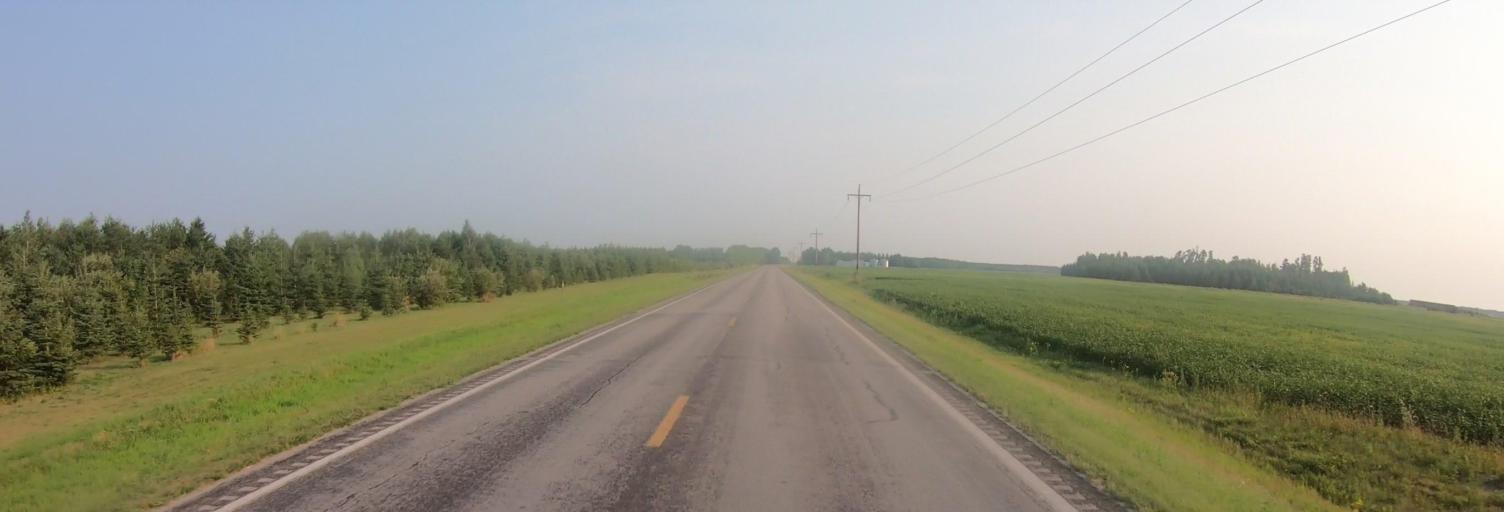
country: US
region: Minnesota
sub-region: Roseau County
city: Warroad
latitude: 48.7873
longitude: -95.3305
